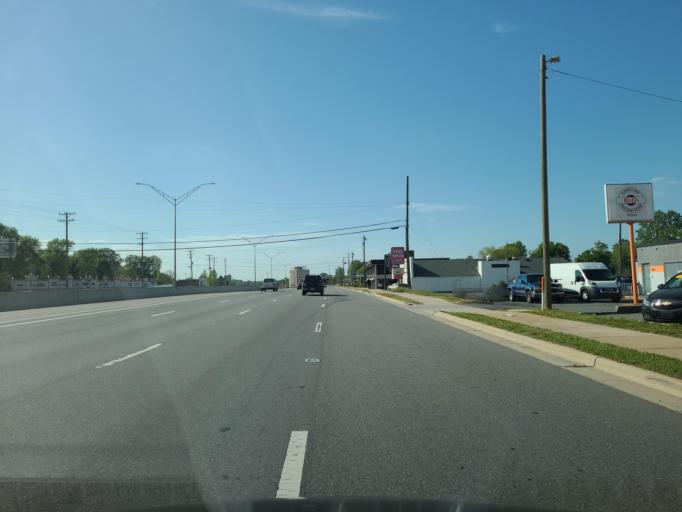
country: US
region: North Carolina
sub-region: Mecklenburg County
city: Charlotte
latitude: 35.1953
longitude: -80.7666
